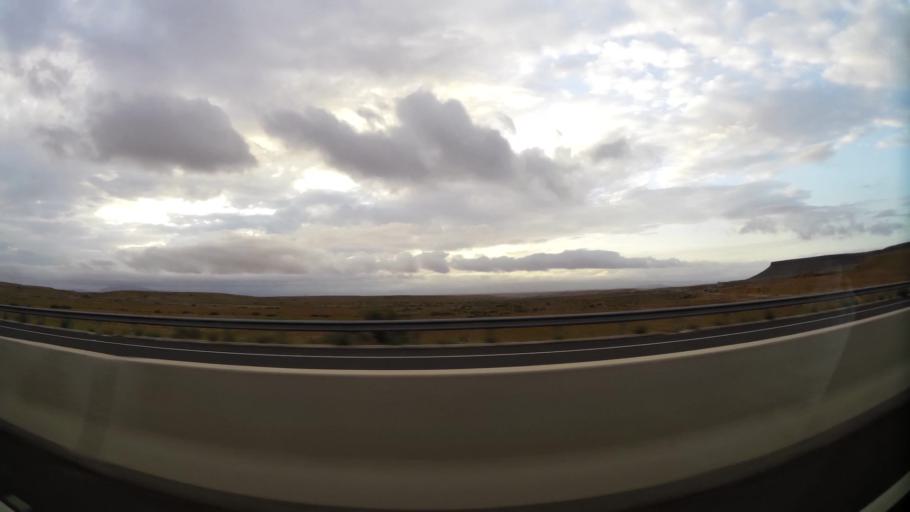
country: MA
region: Oriental
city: Taourirt
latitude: 34.4378
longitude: -3.0856
